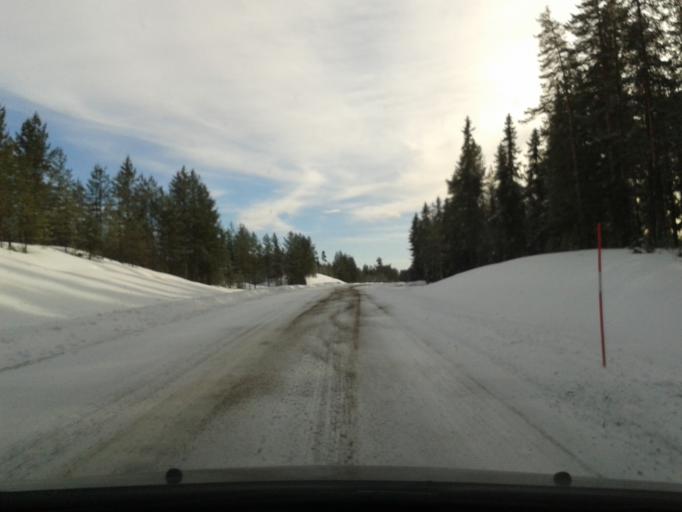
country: SE
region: Vaesterbotten
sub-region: Vilhelmina Kommun
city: Vilhelmina
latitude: 64.5369
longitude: 16.7508
